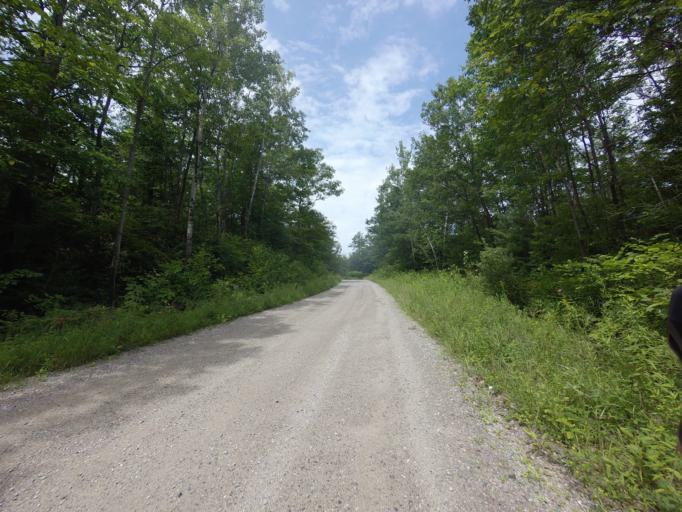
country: CA
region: Ontario
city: Perth
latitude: 44.7528
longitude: -76.6150
